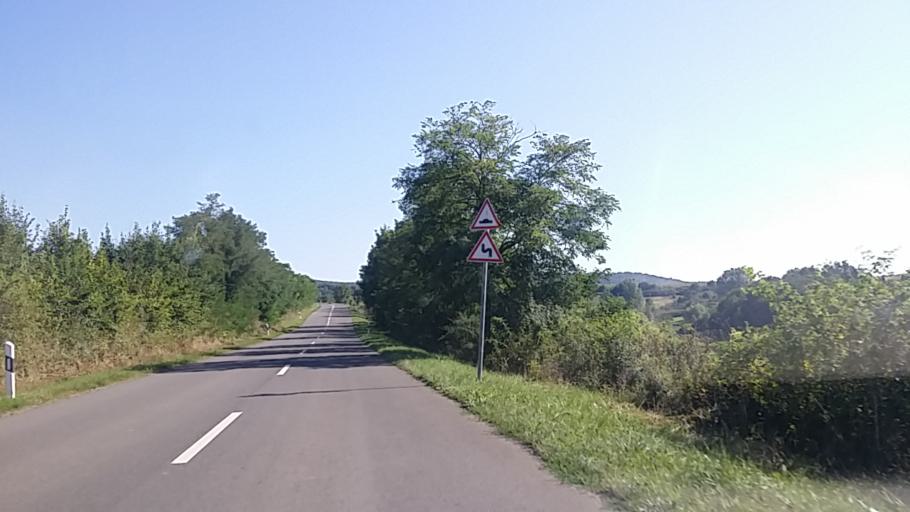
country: HU
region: Nograd
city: Bujak
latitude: 47.9038
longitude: 19.6096
